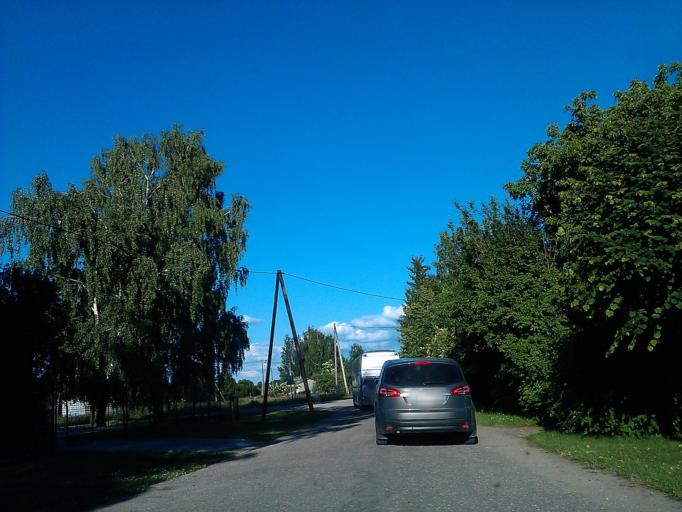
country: LV
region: Varaklani
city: Varaklani
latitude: 56.5717
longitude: 26.8026
